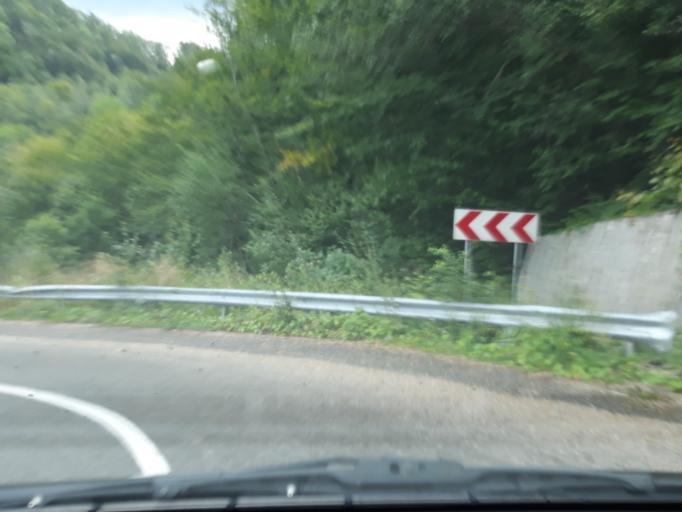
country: RO
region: Bihor
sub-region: Comuna Pietroasa
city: Pietroasa
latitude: 46.6003
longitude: 22.6562
